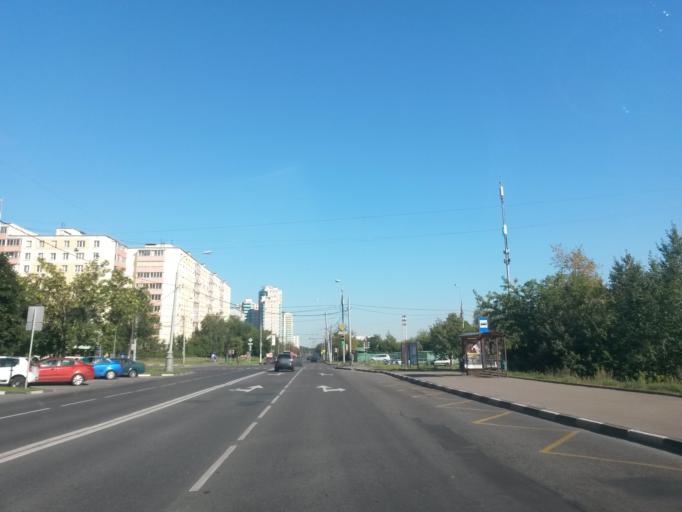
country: RU
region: Moscow
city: Yasenevo
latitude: 55.6006
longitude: 37.5184
